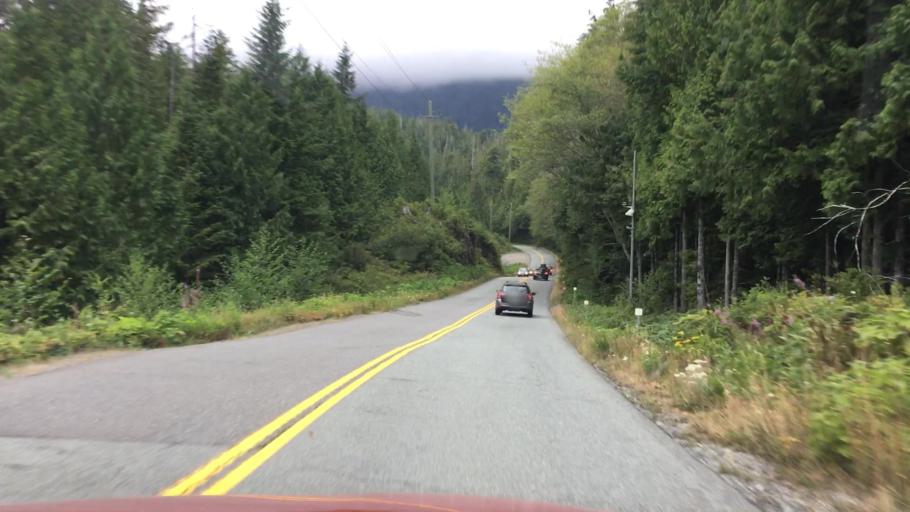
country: CA
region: British Columbia
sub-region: Regional District of Alberni-Clayoquot
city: Ucluelet
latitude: 49.1007
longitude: -125.4526
